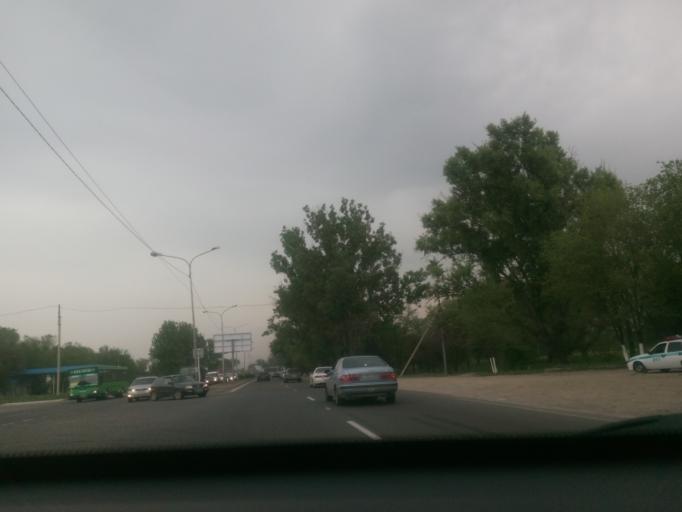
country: KZ
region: Almaty Oblysy
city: Burunday
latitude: 43.2282
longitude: 76.7564
